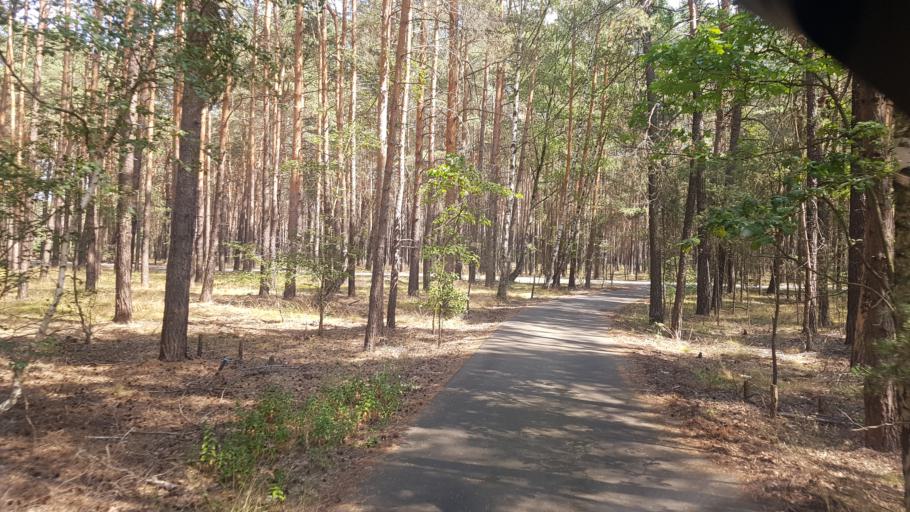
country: DE
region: Brandenburg
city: Spremberg
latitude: 51.6202
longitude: 14.3991
